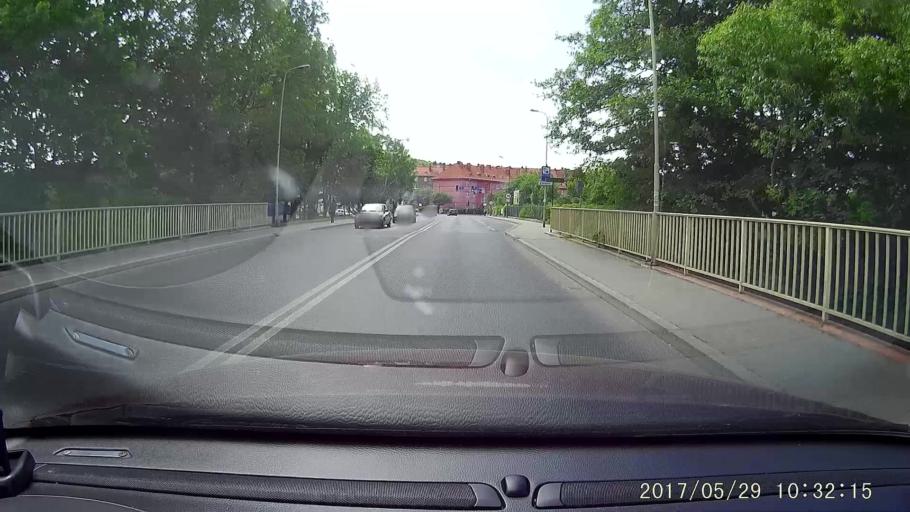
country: PL
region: Lower Silesian Voivodeship
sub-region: Jelenia Gora
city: Jelenia Gora
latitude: 50.9068
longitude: 15.7504
